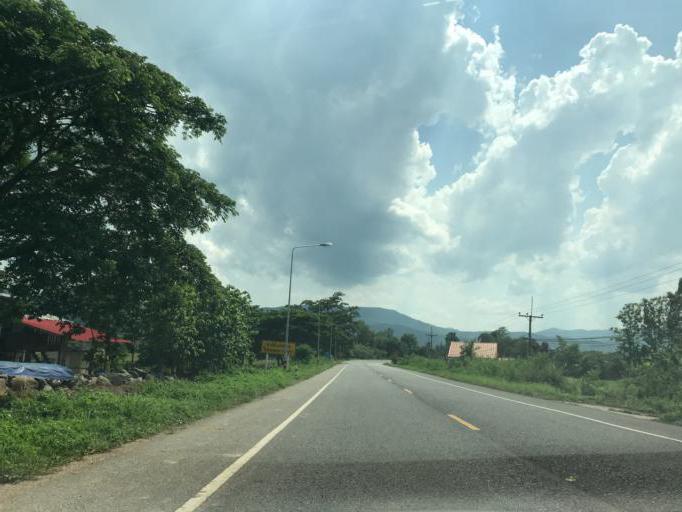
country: TH
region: Phayao
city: Phayao
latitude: 19.0800
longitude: 99.8701
